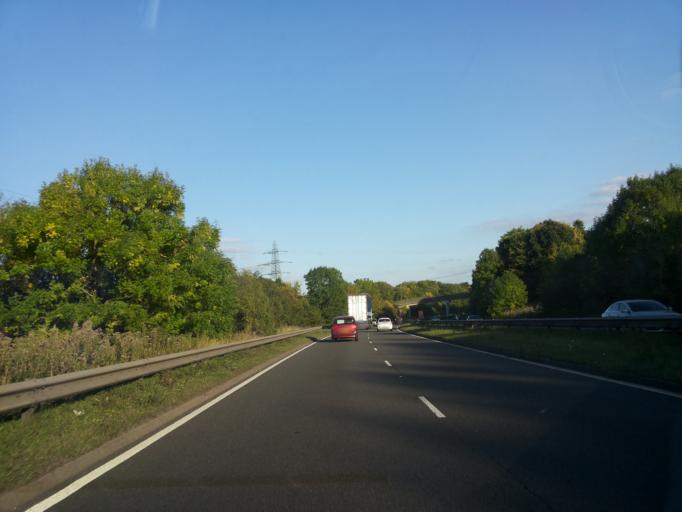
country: GB
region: England
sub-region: Derbyshire
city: Bolsover
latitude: 53.2007
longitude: -1.3348
